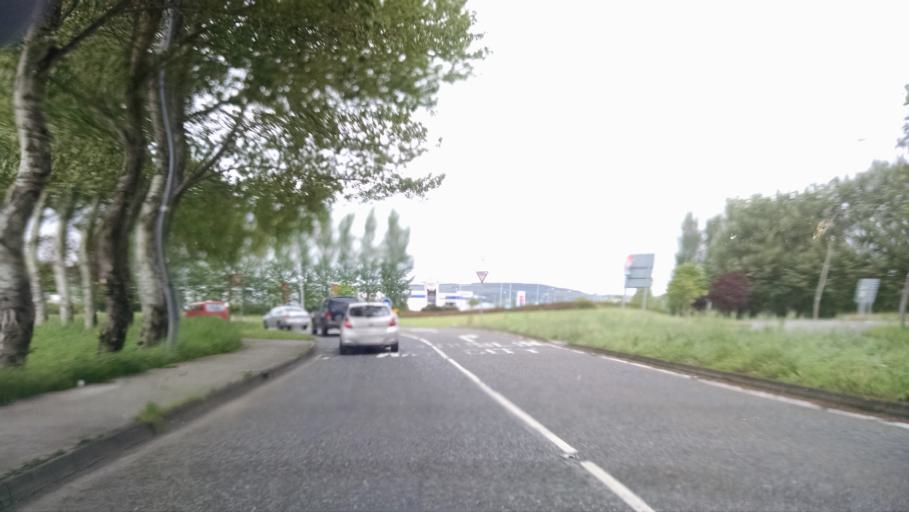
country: IE
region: Munster
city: Moyross
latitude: 52.6735
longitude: -8.6750
